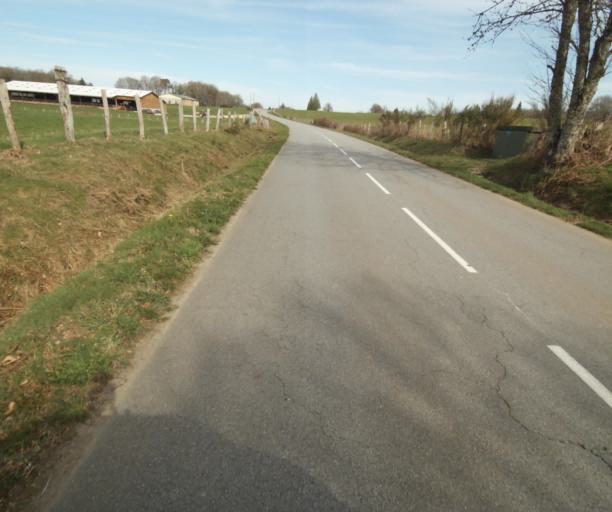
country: FR
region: Limousin
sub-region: Departement de la Correze
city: Correze
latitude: 45.3988
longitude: 1.8271
